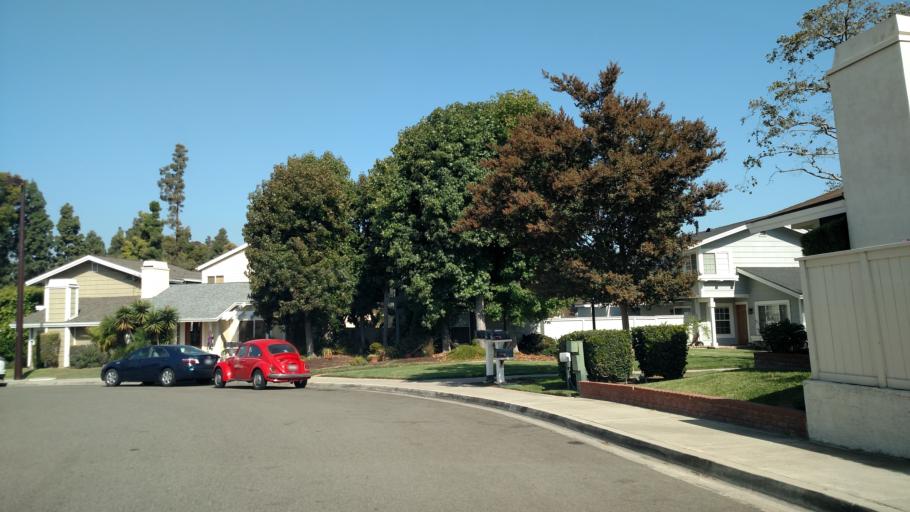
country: US
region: California
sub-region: Orange County
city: Irvine
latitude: 33.6696
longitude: -117.8151
